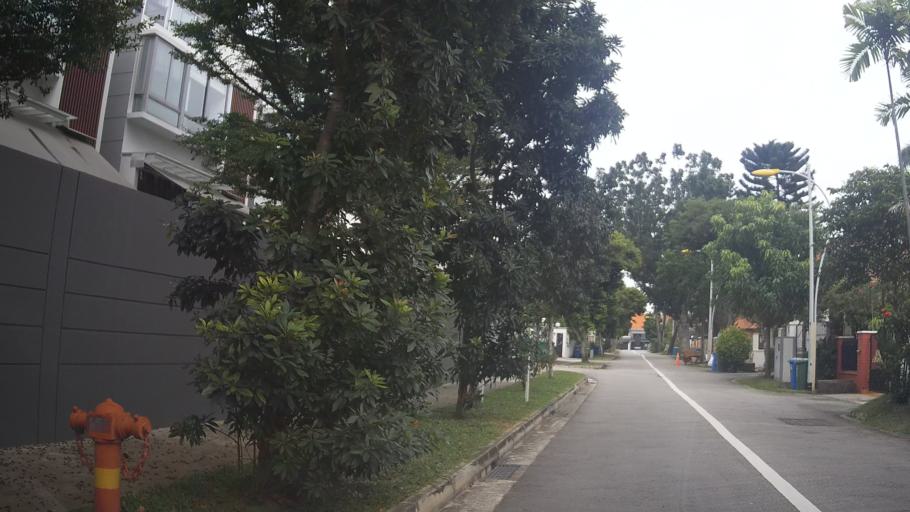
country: SG
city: Singapore
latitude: 1.3302
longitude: 103.8716
